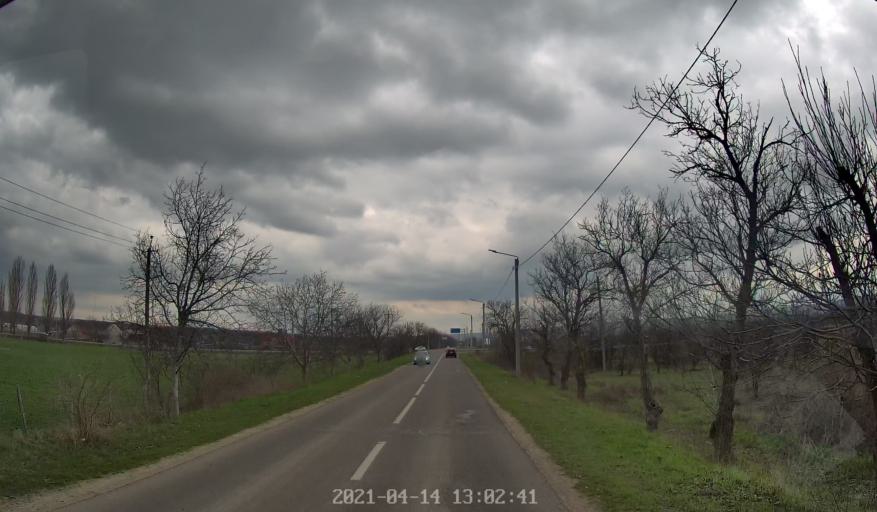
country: MD
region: Chisinau
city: Vadul lui Voda
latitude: 47.1212
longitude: 29.1111
